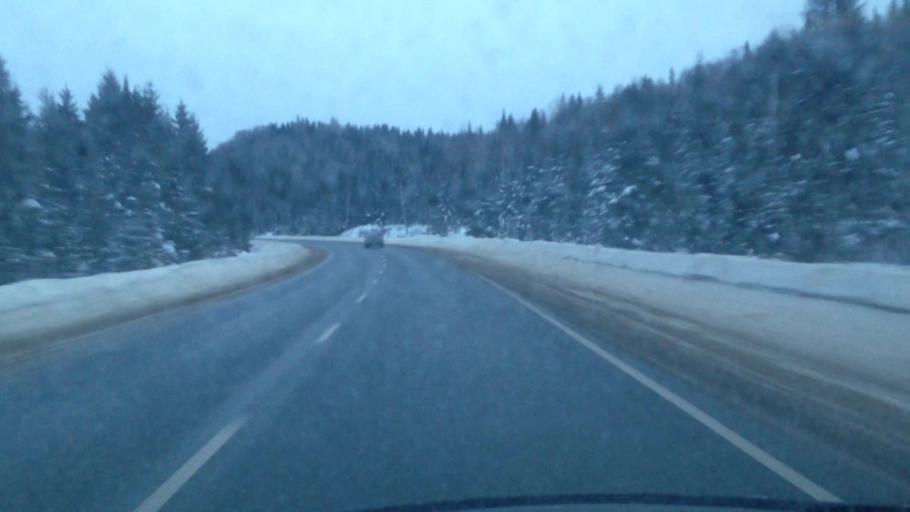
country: CA
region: Quebec
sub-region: Laurentides
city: Sainte-Agathe-des-Monts
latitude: 46.1132
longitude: -74.4271
